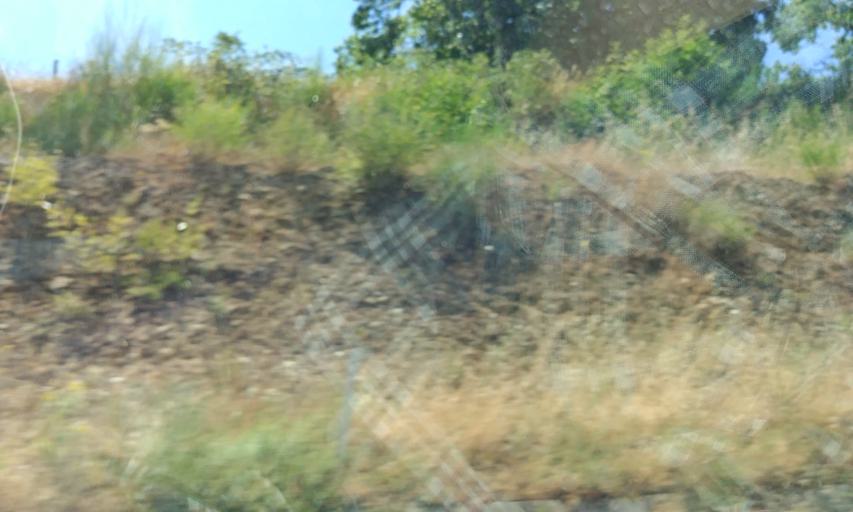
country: PT
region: Braganca
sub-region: Macedo de Cavaleiros
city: Macedo de Cavaleiros
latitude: 41.5704
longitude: -6.9804
